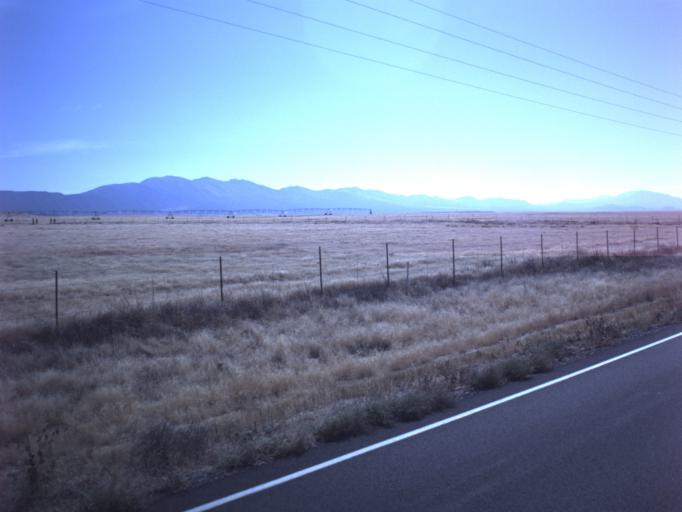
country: US
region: Utah
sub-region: Tooele County
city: Grantsville
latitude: 40.3912
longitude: -112.7475
